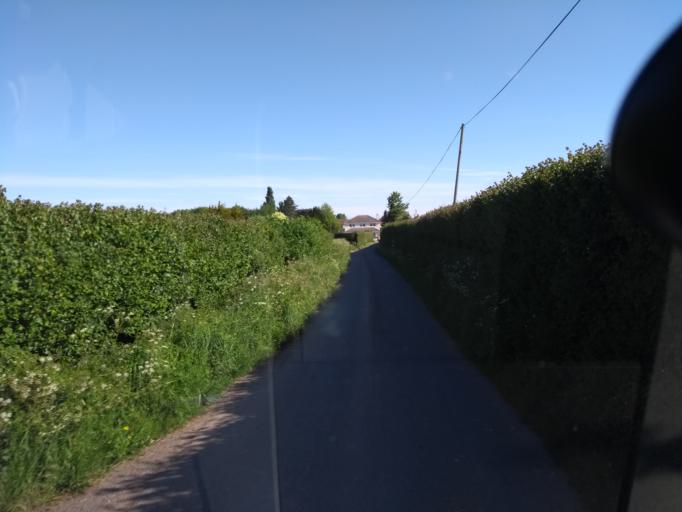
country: GB
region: England
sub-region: Somerset
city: Bridgwater
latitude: 51.1418
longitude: -3.0353
